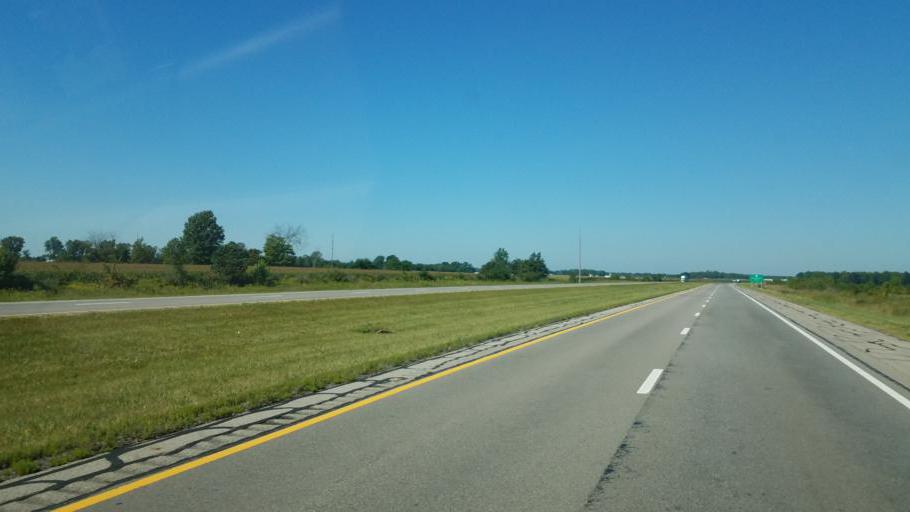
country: US
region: Ohio
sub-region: Crawford County
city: Galion
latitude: 40.7621
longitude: -82.8264
